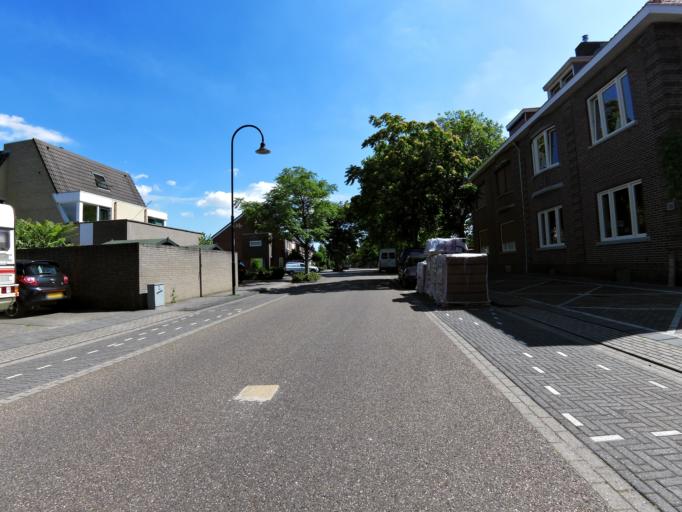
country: NL
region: Limburg
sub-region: Gemeente Kerkrade
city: Kerkrade
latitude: 50.8663
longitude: 6.0733
